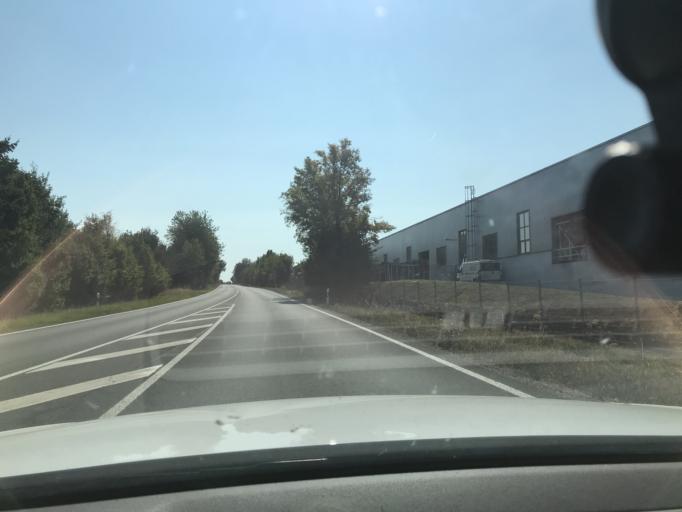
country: DE
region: Bavaria
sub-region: Upper Palatinate
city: Auerbach
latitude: 49.6881
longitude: 11.6258
